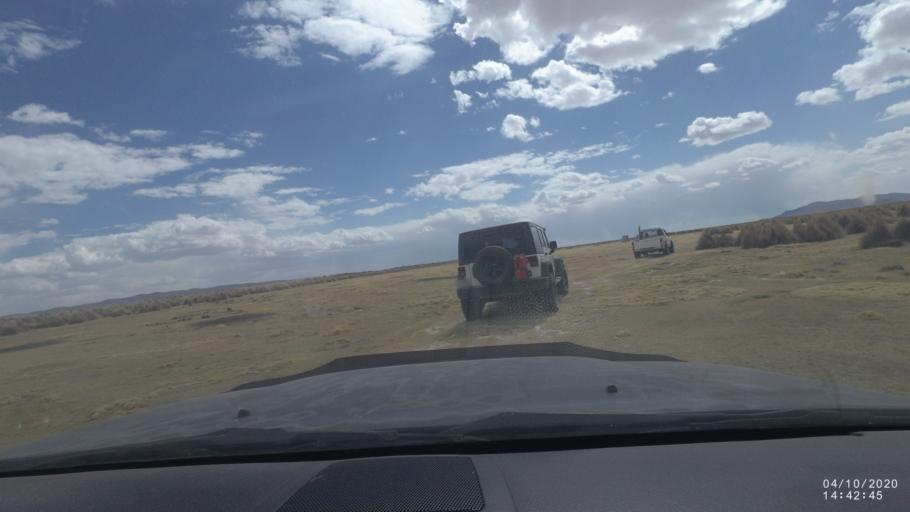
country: BO
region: Oruro
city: Poopo
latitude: -18.6869
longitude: -67.4917
